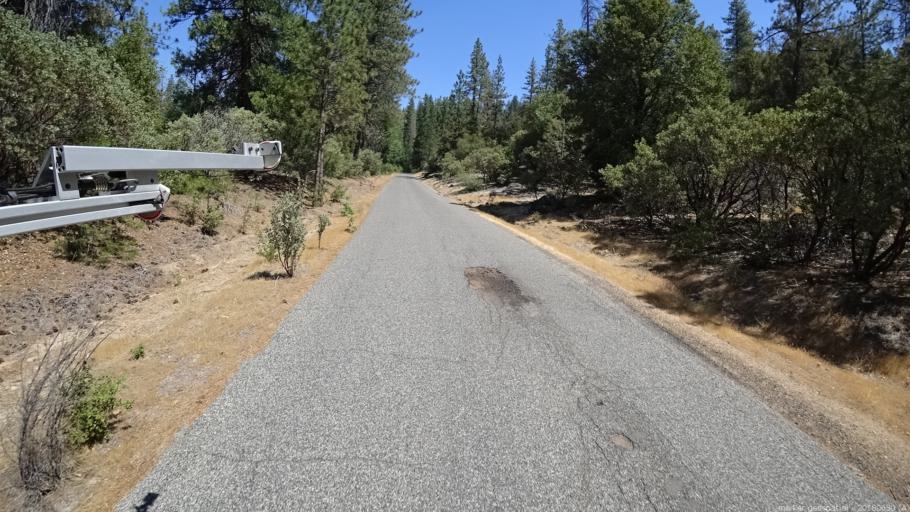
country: US
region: California
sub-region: Madera County
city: Oakhurst
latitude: 37.3577
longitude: -119.3444
